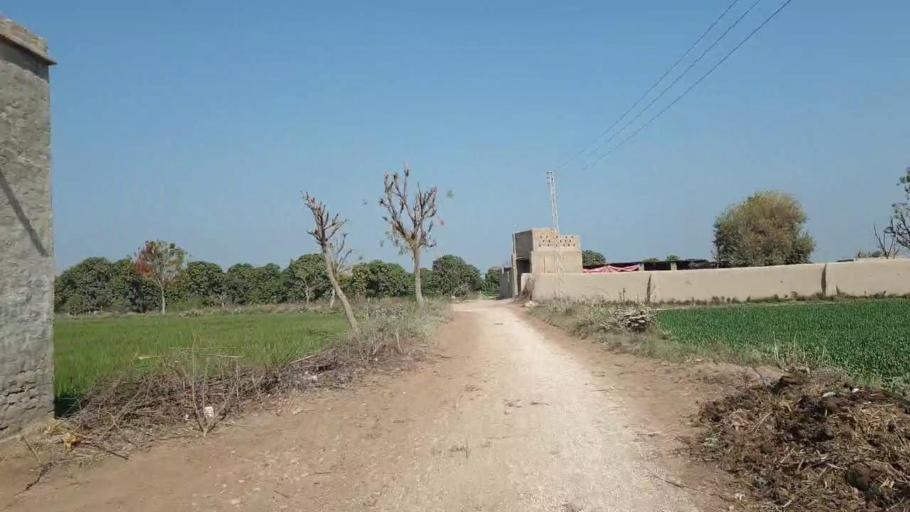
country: PK
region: Sindh
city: Hala
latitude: 25.9095
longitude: 68.4318
